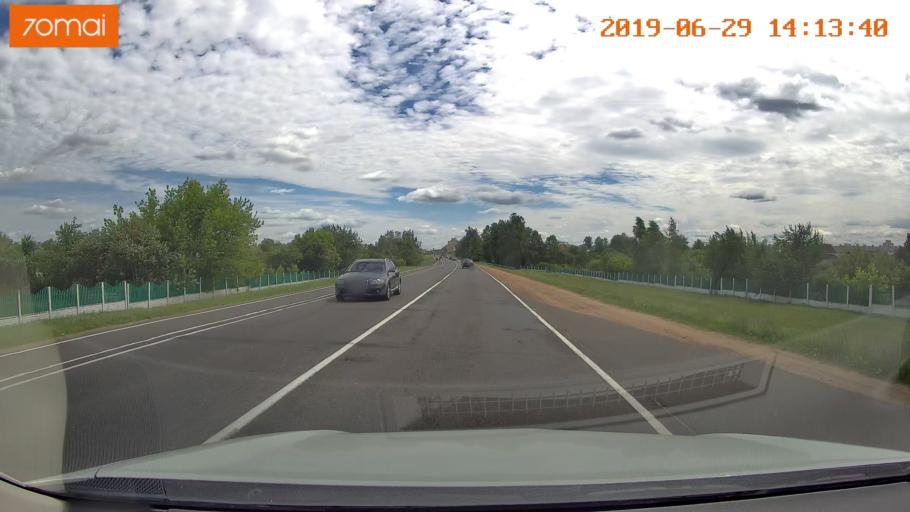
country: BY
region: Minsk
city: Salihorsk
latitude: 52.8014
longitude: 27.5116
